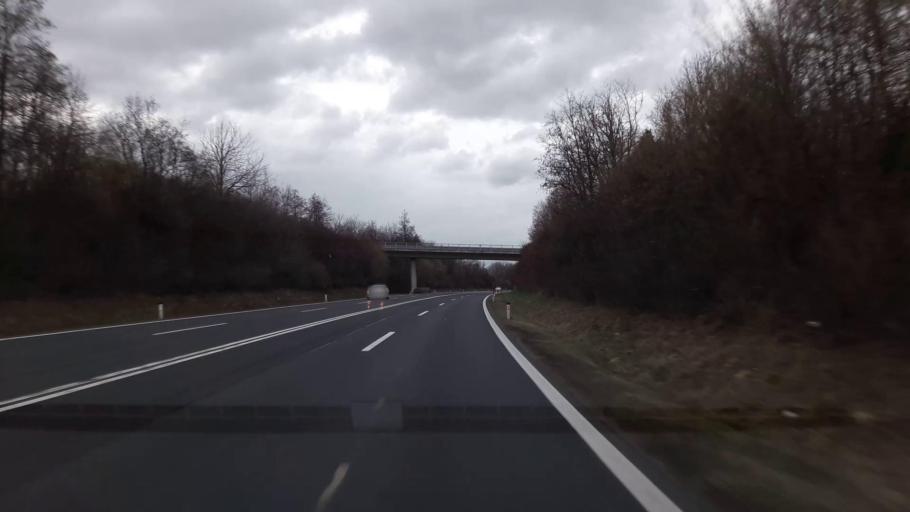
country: AT
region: Burgenland
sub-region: Politischer Bezirk Mattersburg
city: Mattersburg
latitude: 47.7290
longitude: 16.3731
